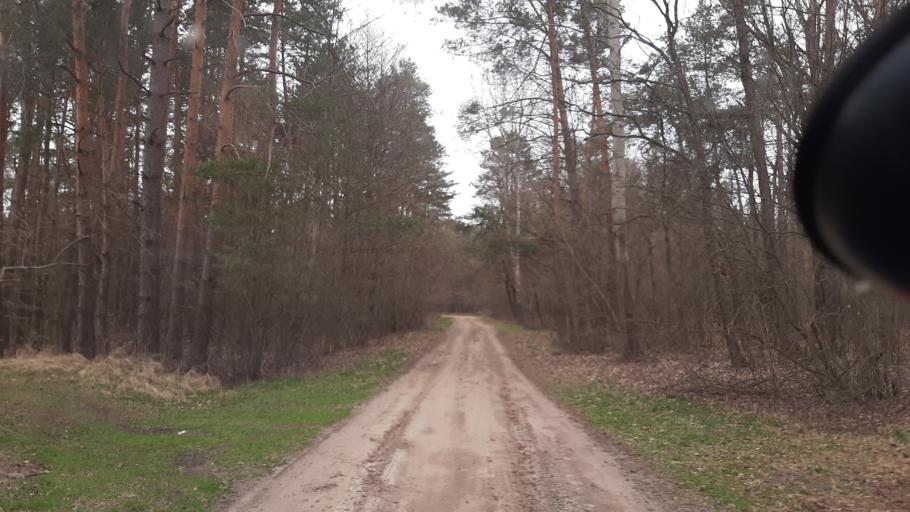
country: PL
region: Lublin Voivodeship
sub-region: Powiat lubartowski
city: Abramow
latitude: 51.4421
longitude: 22.3451
